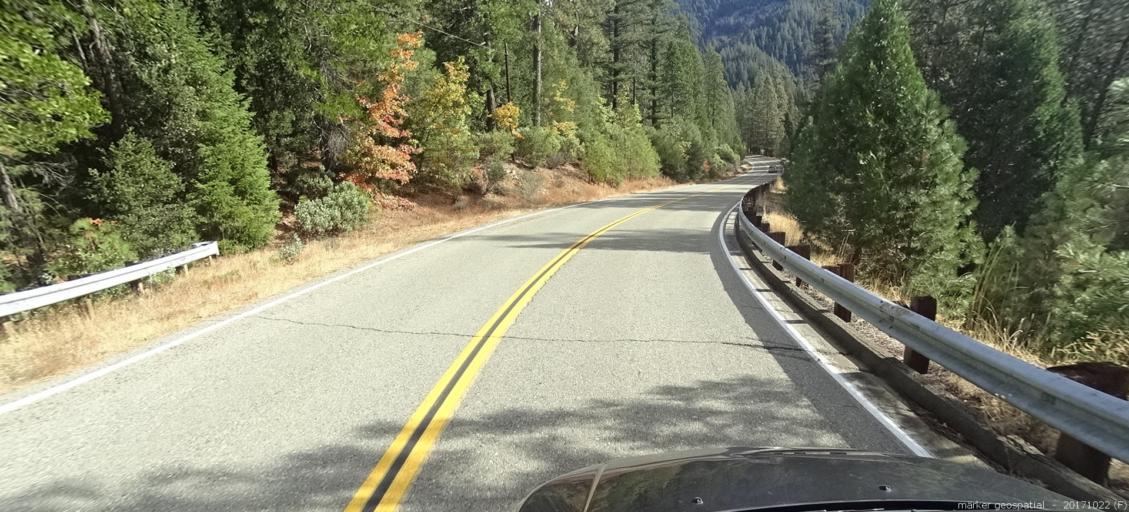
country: US
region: California
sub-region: Siskiyou County
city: Dunsmuir
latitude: 41.0654
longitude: -122.3667
